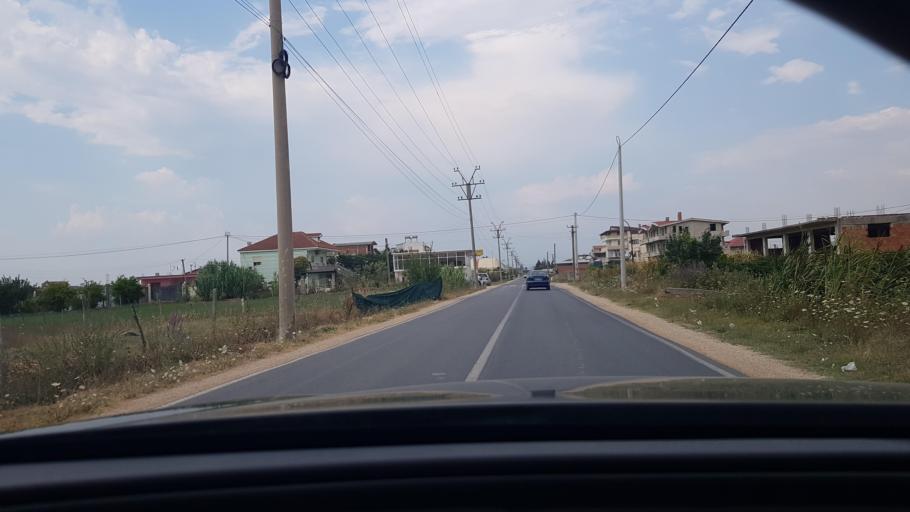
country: AL
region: Durres
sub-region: Rrethi i Durresit
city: Sukth
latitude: 41.4039
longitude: 19.5467
